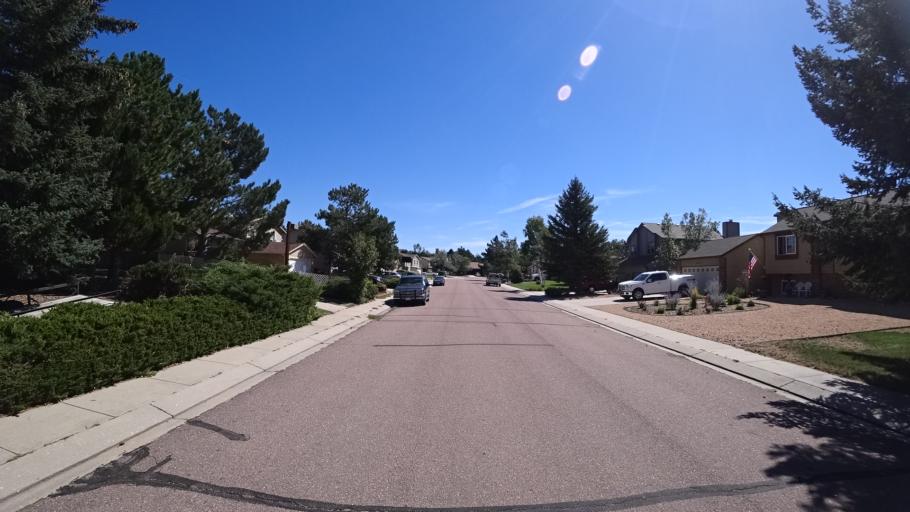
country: US
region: Colorado
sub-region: El Paso County
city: Black Forest
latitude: 38.9518
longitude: -104.7536
